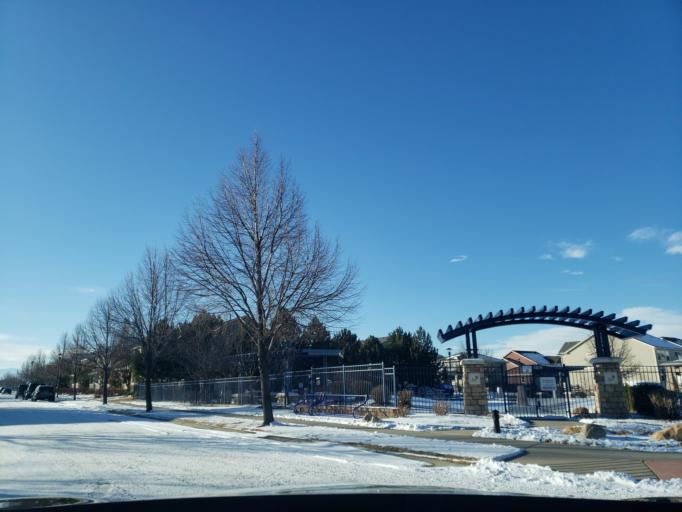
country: US
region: Colorado
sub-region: Larimer County
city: Fort Collins
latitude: 40.5136
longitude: -105.0073
